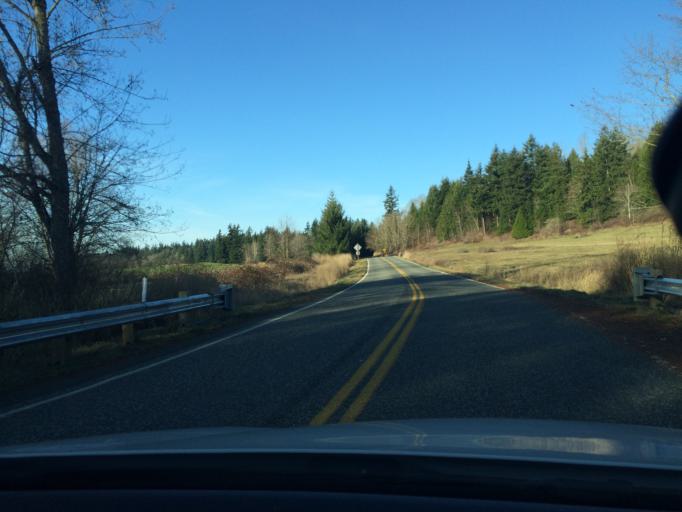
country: US
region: Washington
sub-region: Whatcom County
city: Everson
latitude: 48.8476
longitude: -122.3998
